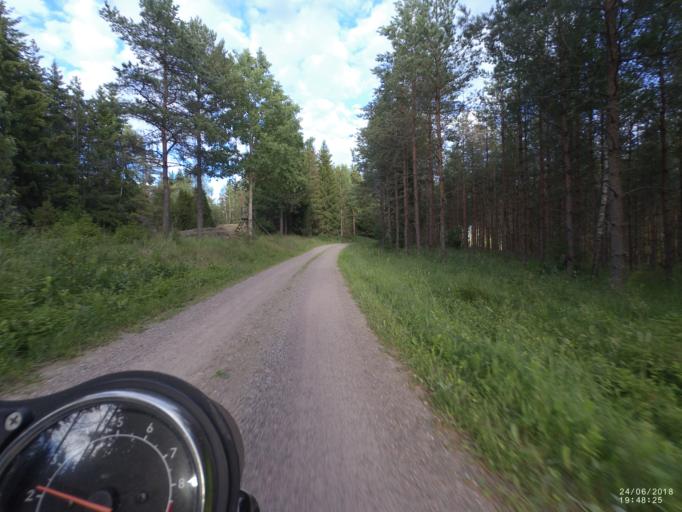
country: SE
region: Soedermanland
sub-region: Oxelosunds Kommun
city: Oxelosund
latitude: 58.7837
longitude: 17.1331
